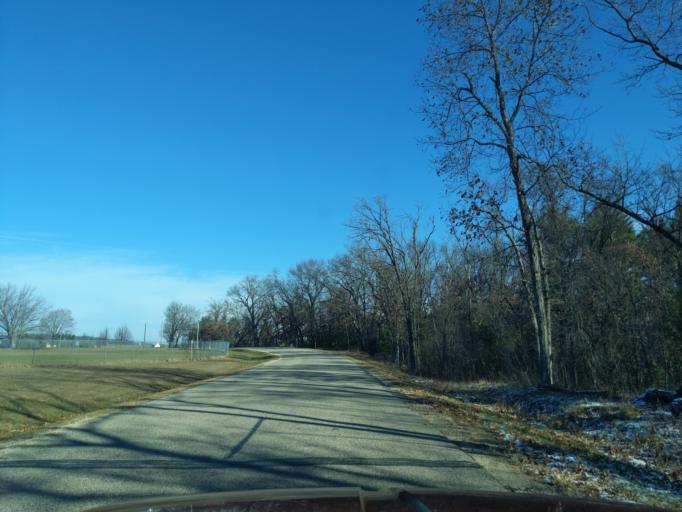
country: US
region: Wisconsin
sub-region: Waushara County
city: Silver Lake
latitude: 44.0909
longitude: -89.1896
